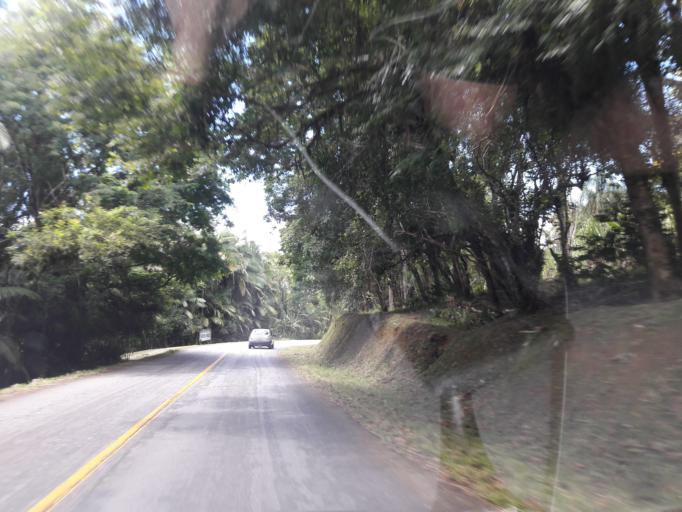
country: BR
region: Parana
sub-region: Antonina
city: Antonina
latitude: -25.4334
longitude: -48.7978
